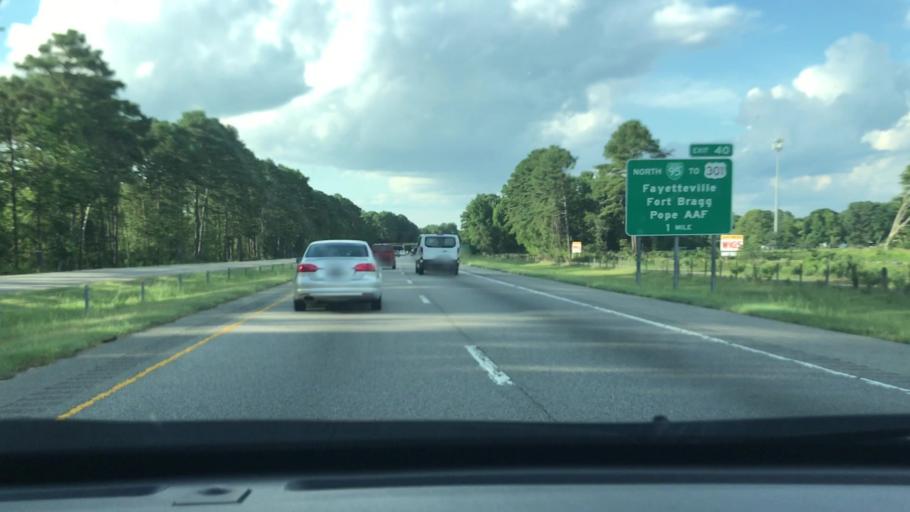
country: US
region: North Carolina
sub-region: Cumberland County
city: Hope Mills
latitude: 34.9036
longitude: -78.9576
